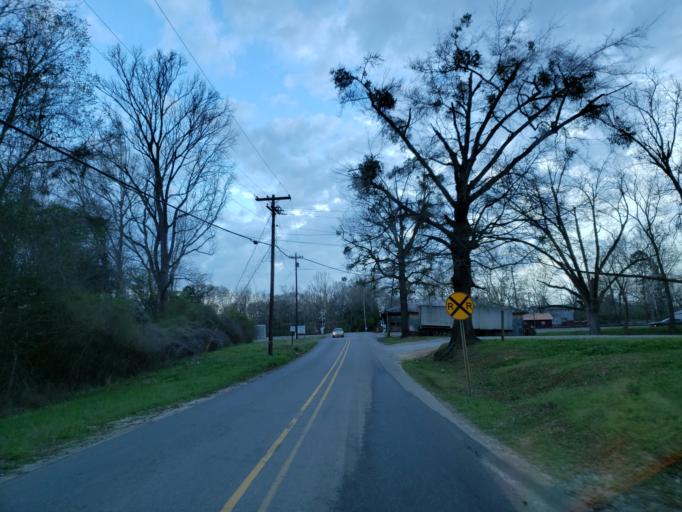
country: US
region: Mississippi
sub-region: Lauderdale County
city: Marion
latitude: 32.4165
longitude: -88.5063
